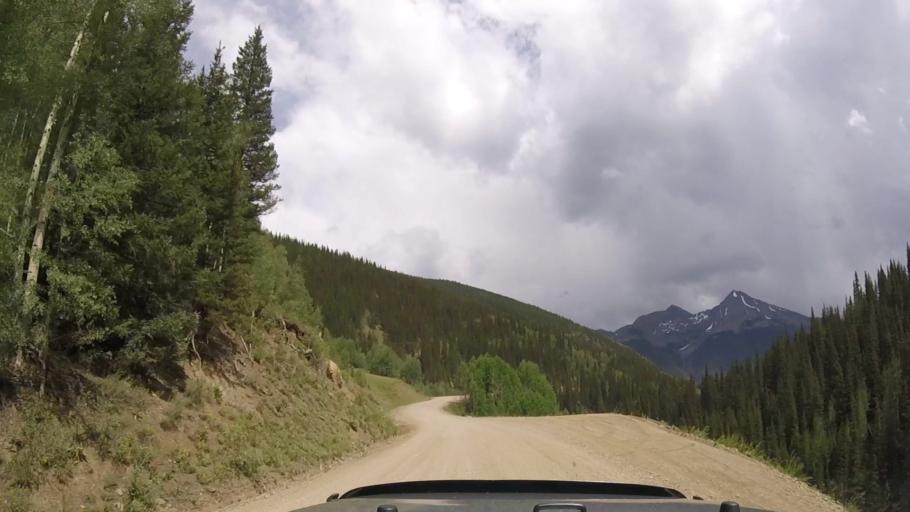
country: US
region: Colorado
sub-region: San Juan County
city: Silverton
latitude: 37.8346
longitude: -107.6756
